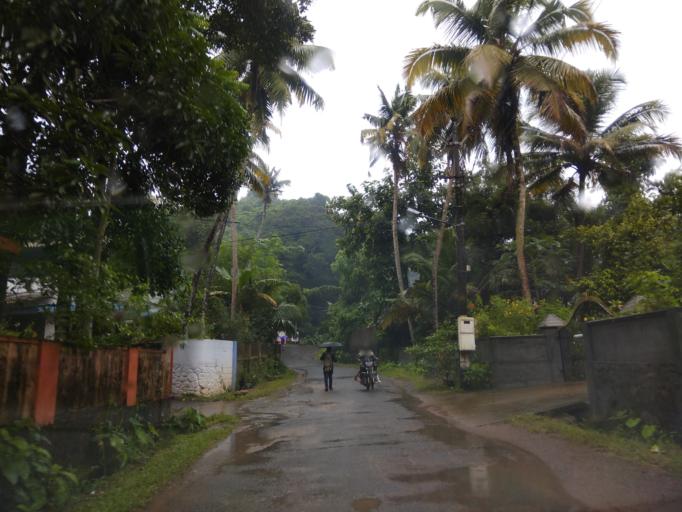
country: IN
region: Kerala
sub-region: Ernakulam
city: Perumpavur
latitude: 10.1110
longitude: 76.4995
